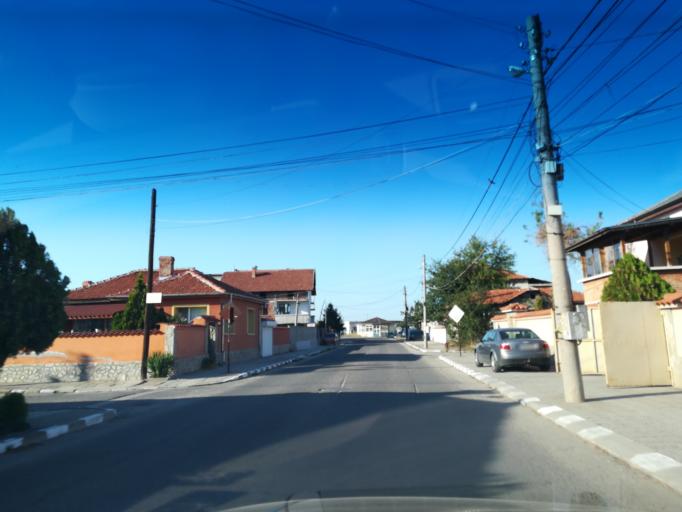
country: BG
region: Stara Zagora
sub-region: Obshtina Chirpan
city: Chirpan
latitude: 42.1059
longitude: 25.2212
